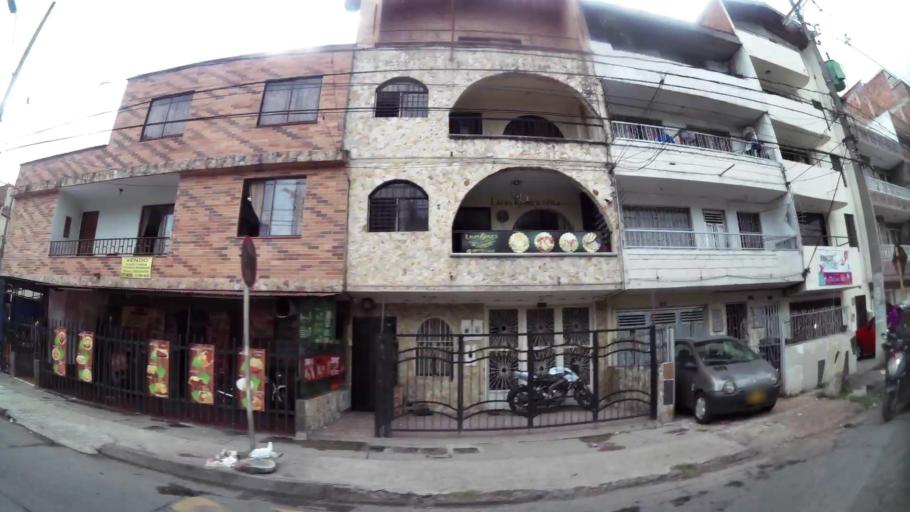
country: CO
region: Antioquia
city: Itagui
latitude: 6.1862
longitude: -75.5942
